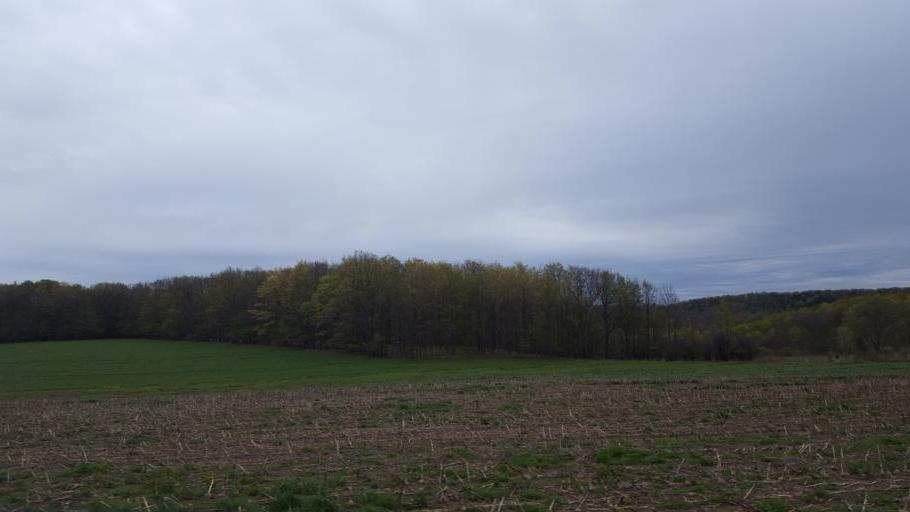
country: US
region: Pennsylvania
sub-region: Tioga County
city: Westfield
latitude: 42.0597
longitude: -77.4639
